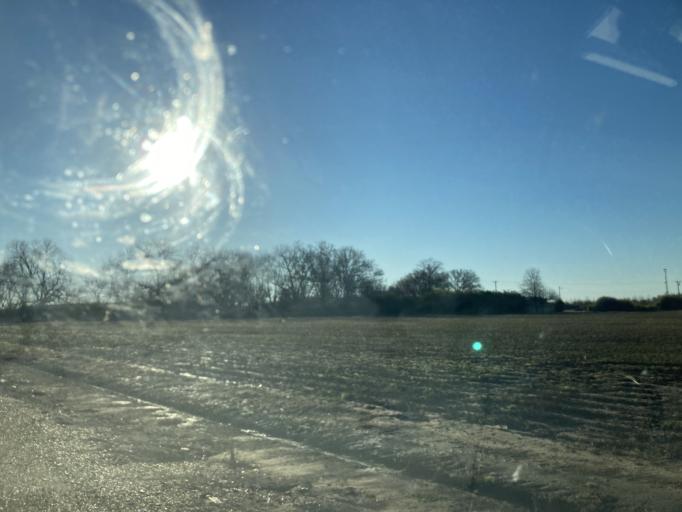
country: US
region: Mississippi
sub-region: Yazoo County
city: Yazoo City
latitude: 32.9286
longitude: -90.5899
